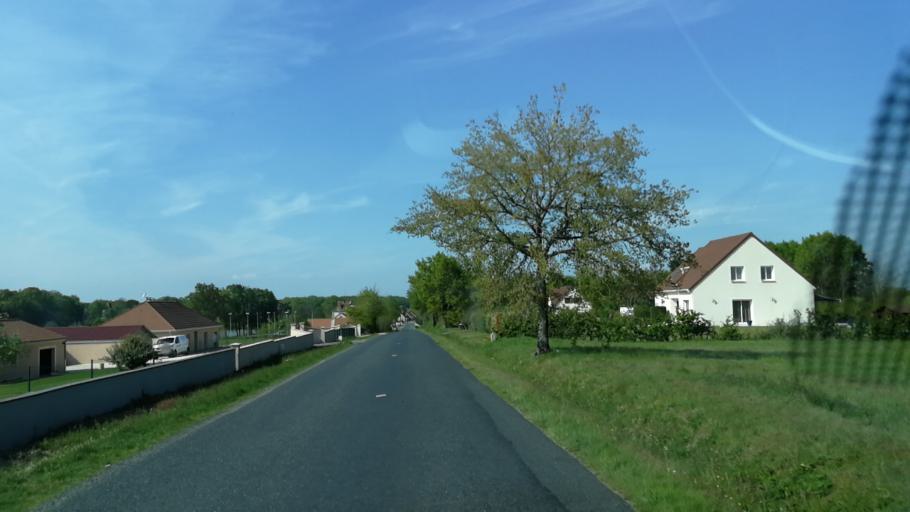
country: FR
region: Auvergne
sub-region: Departement de l'Allier
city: Neuilly-le-Real
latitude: 46.4838
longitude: 3.5227
